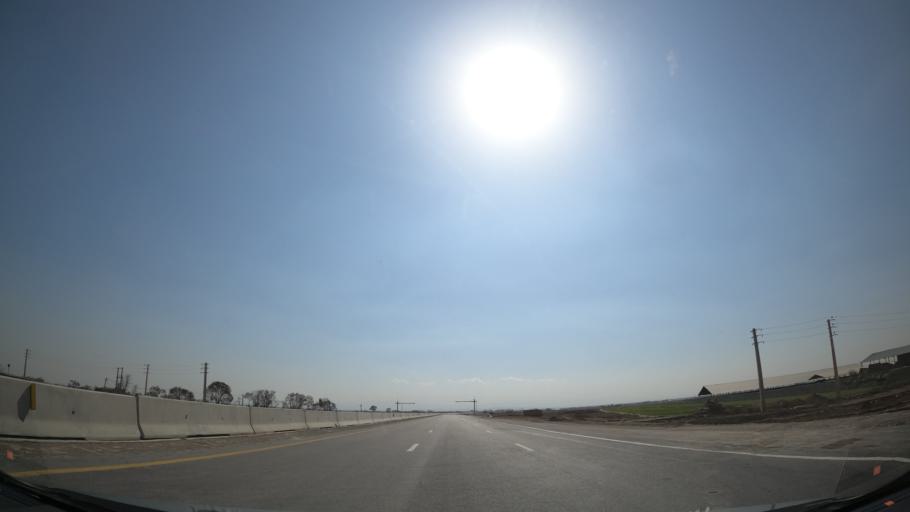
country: IR
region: Qazvin
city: Abyek
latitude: 35.9920
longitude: 50.4620
